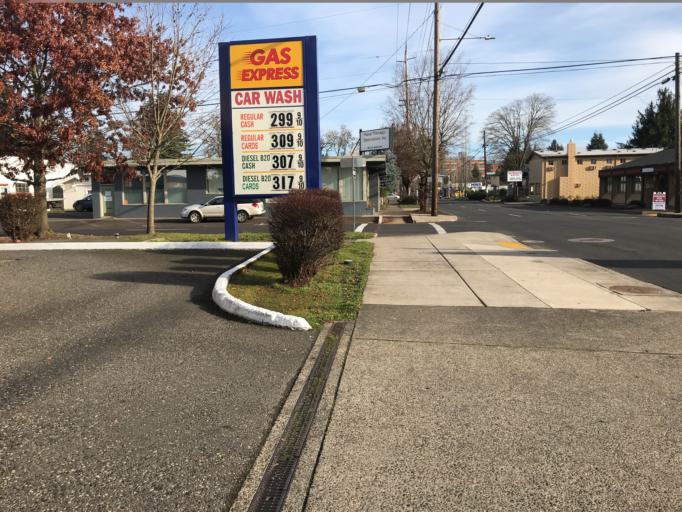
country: US
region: Oregon
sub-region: Washington County
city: Hillsboro
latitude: 45.5201
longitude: -122.9847
